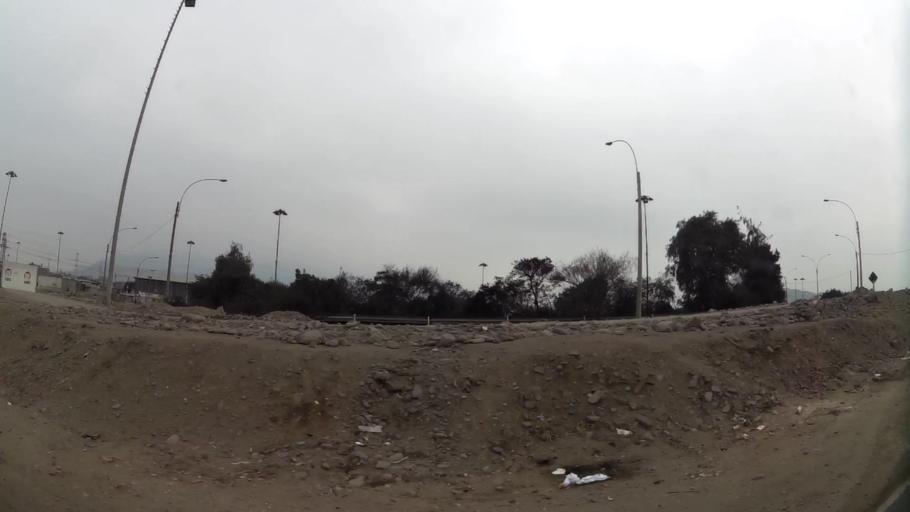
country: PE
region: Lima
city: Lima
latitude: -12.0330
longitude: -76.9931
